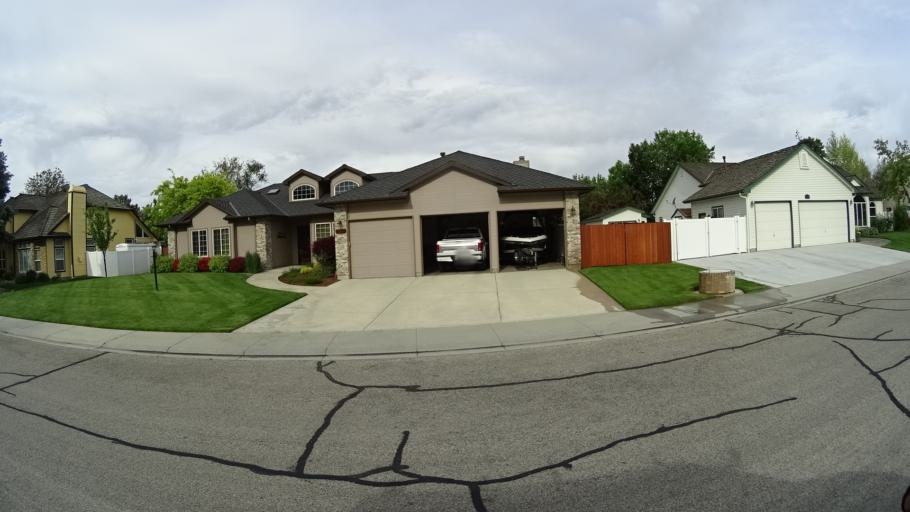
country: US
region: Idaho
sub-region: Ada County
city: Meridian
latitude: 43.5887
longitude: -116.3889
